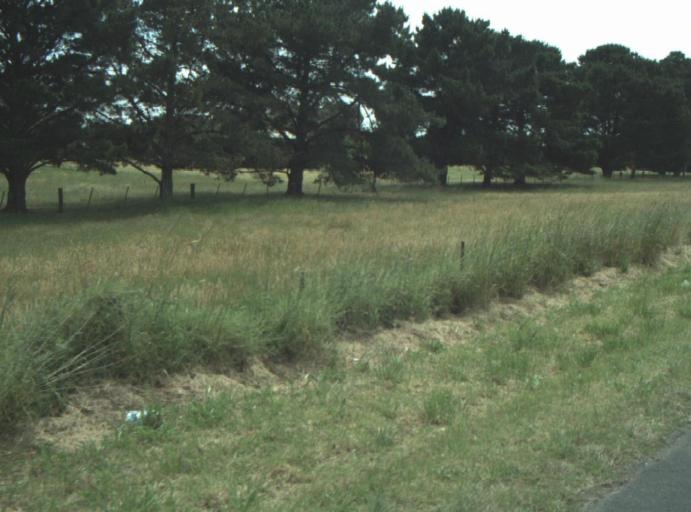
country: AU
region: Victoria
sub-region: Greater Geelong
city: Clifton Springs
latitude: -38.1354
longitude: 144.6133
